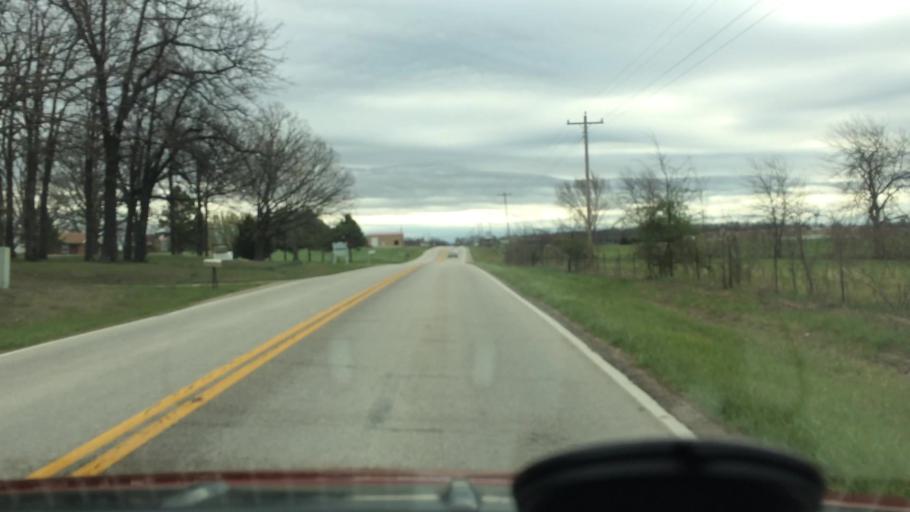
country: US
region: Missouri
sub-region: Webster County
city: Marshfield
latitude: 37.3402
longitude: -92.9469
